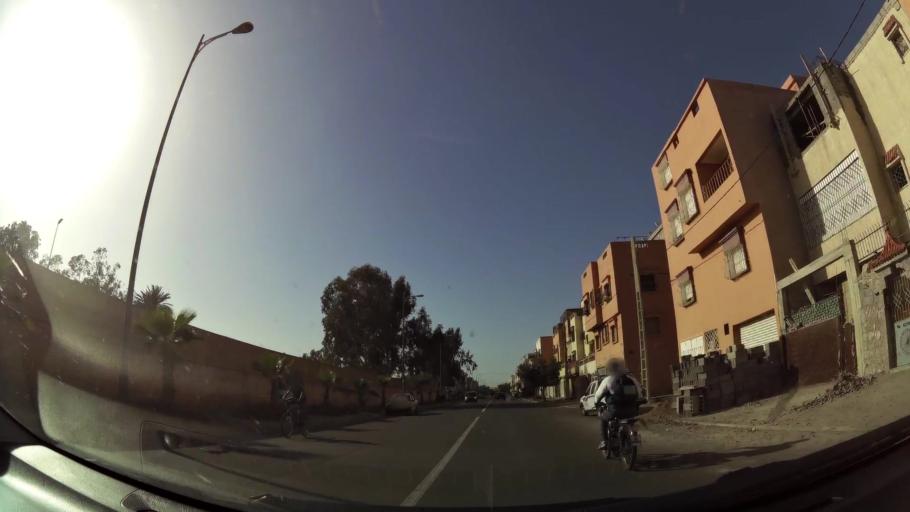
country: MA
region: Souss-Massa-Draa
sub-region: Inezgane-Ait Mellou
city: Inezgane
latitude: 30.3652
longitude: -9.5278
